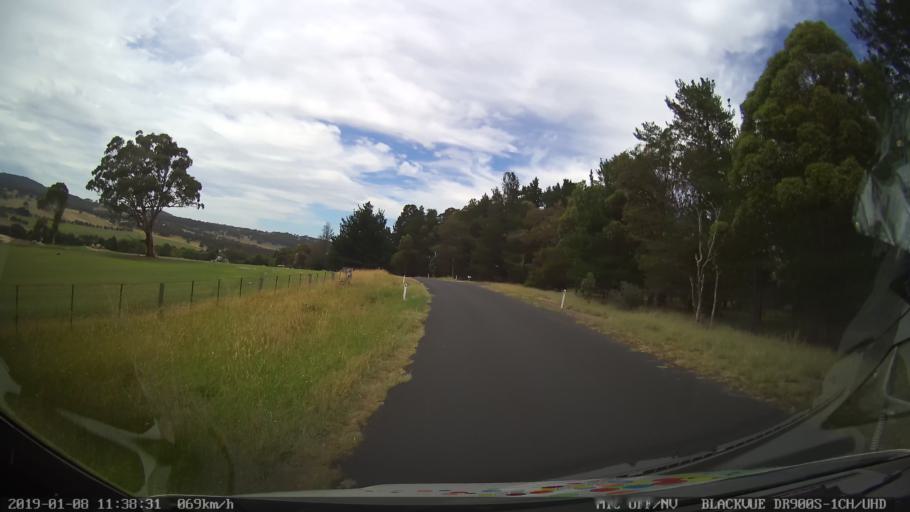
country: AU
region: New South Wales
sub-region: Armidale Dumaresq
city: Armidale
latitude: -30.3618
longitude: 151.5550
